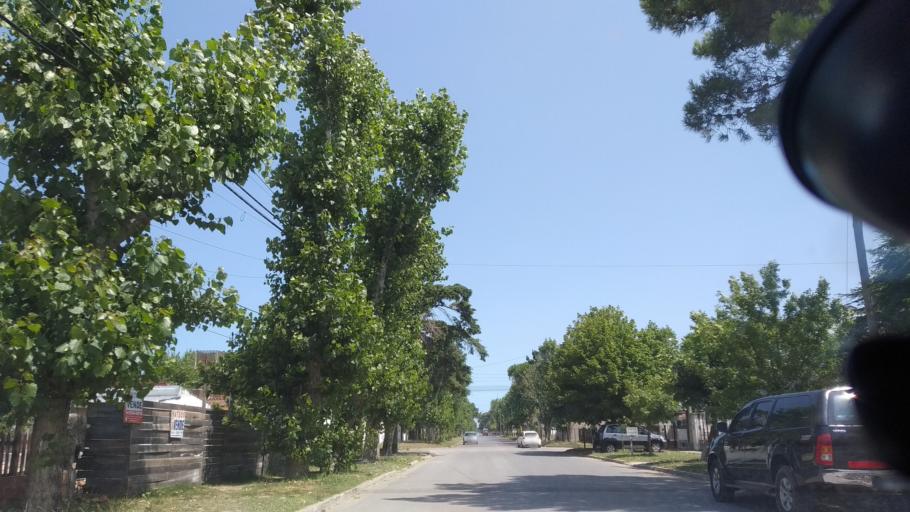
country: AR
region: Buenos Aires
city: Mar del Tuyu
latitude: -36.5716
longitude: -56.6940
